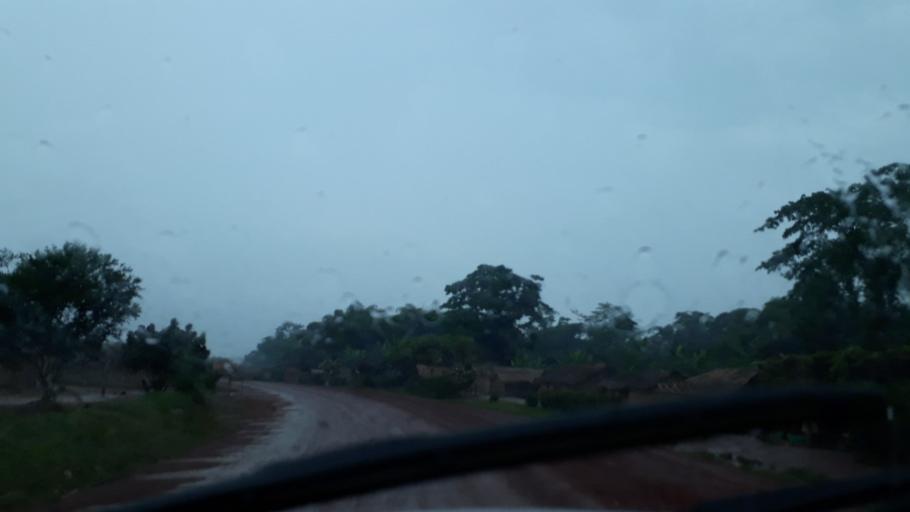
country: CD
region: Eastern Province
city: Kisangani
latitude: 0.4671
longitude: 25.5371
